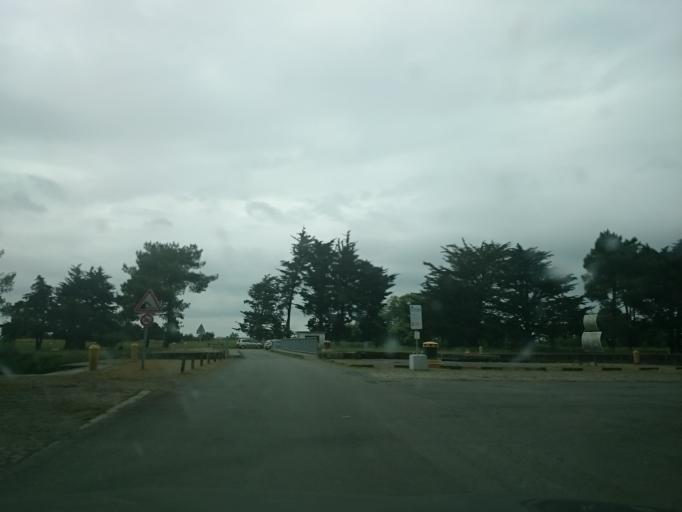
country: FR
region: Pays de la Loire
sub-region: Departement de la Loire-Atlantique
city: Le Pellerin
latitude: 47.2073
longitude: -1.7855
